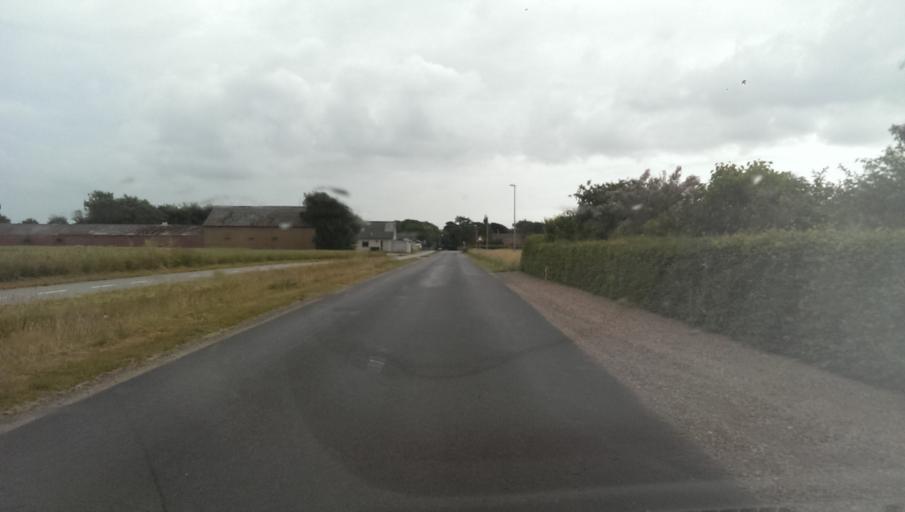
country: DK
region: South Denmark
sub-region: Esbjerg Kommune
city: Bramming
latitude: 55.4390
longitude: 8.7211
